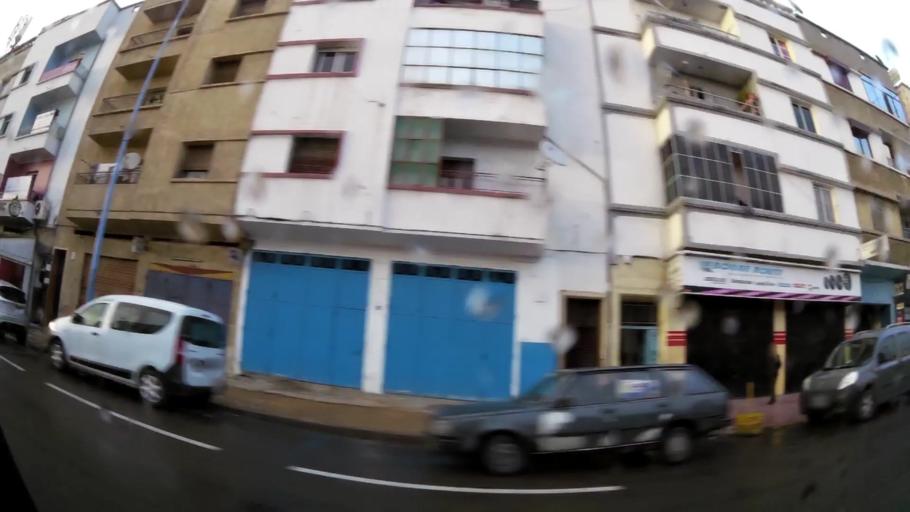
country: MA
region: Grand Casablanca
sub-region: Casablanca
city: Casablanca
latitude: 33.5835
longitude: -7.5700
